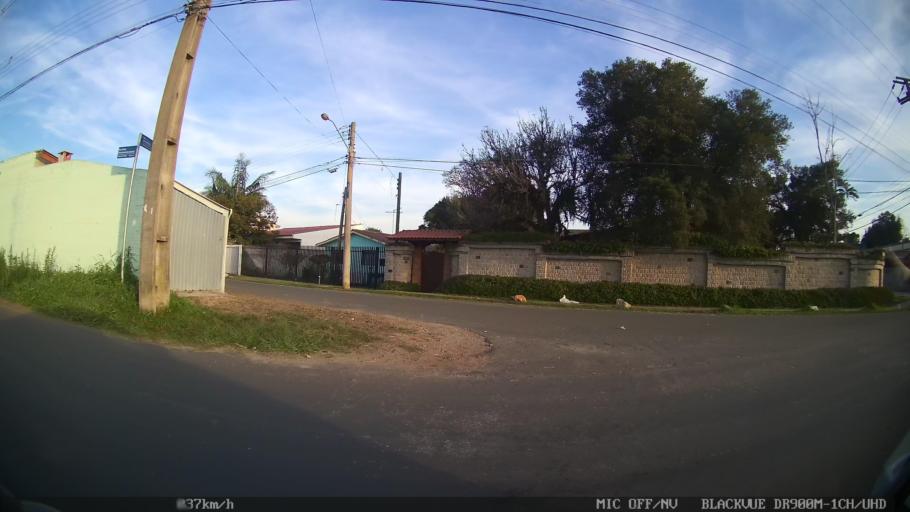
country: BR
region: Parana
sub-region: Pinhais
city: Pinhais
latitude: -25.4394
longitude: -49.1723
